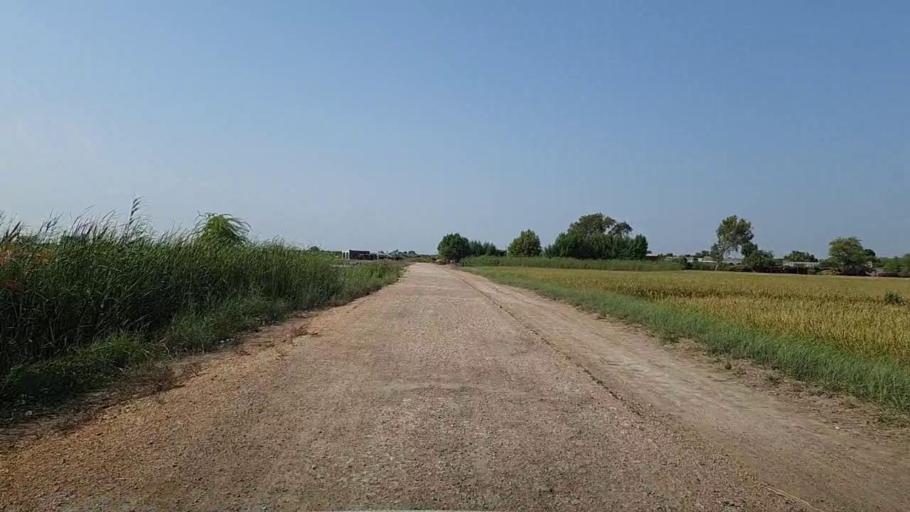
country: PK
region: Sindh
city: Kario
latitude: 24.7944
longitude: 68.5353
